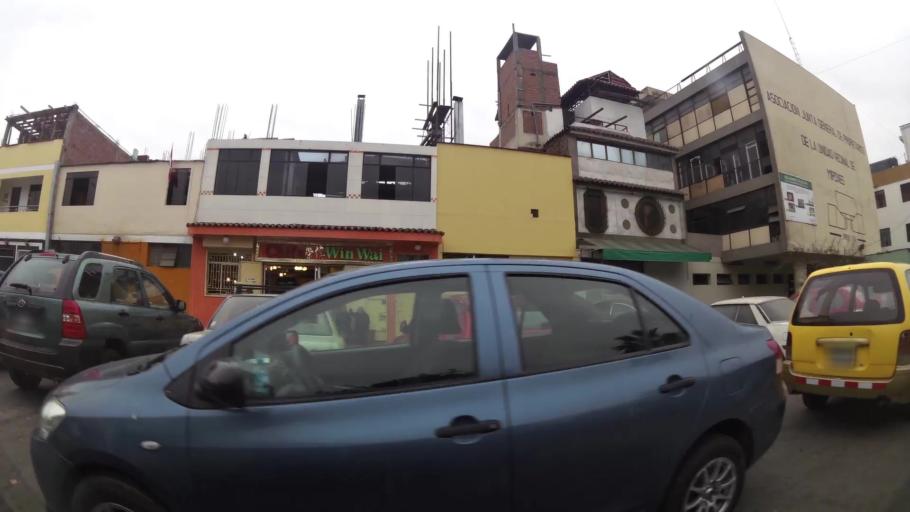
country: PE
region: Lima
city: Lima
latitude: -12.0515
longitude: -77.0673
